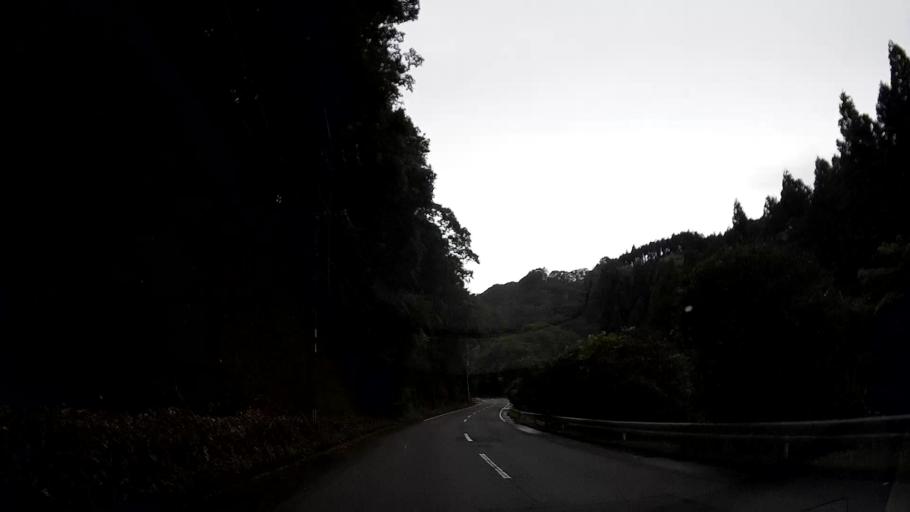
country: JP
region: Kumamoto
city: Kikuchi
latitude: 33.0813
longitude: 130.9385
